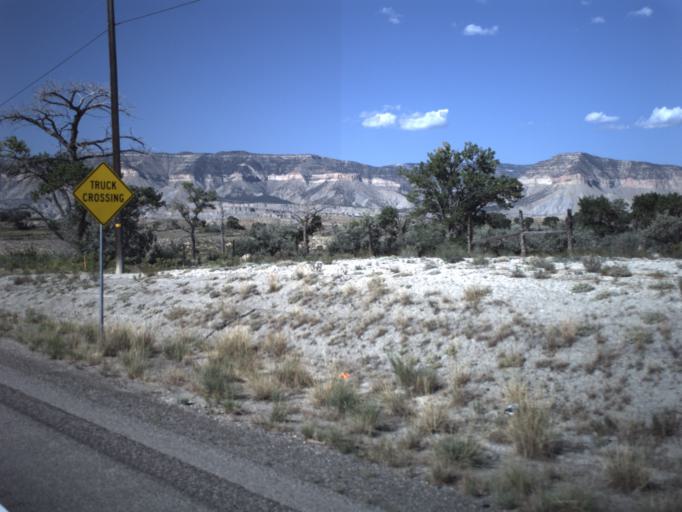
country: US
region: Utah
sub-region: Emery County
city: Ferron
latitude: 39.1085
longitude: -111.1275
